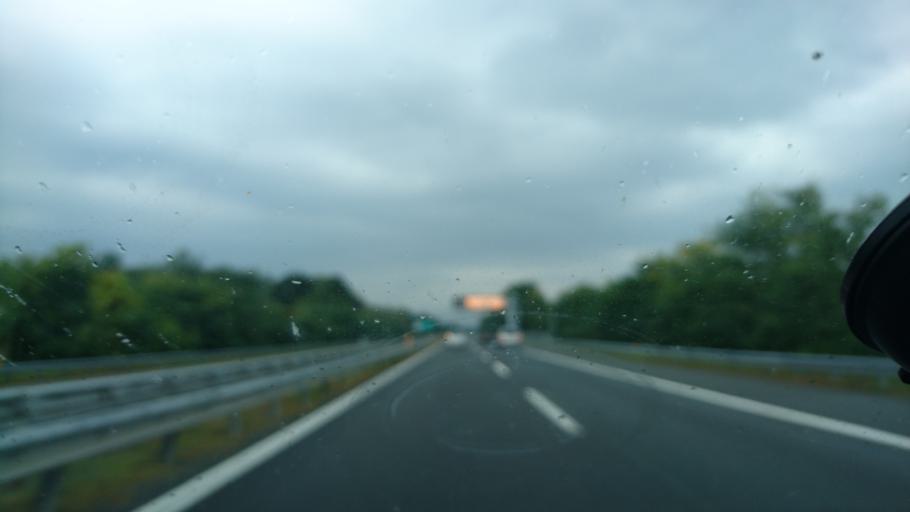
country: IT
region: Piedmont
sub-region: Provincia di Novara
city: Ghemme
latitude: 45.5898
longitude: 8.4036
